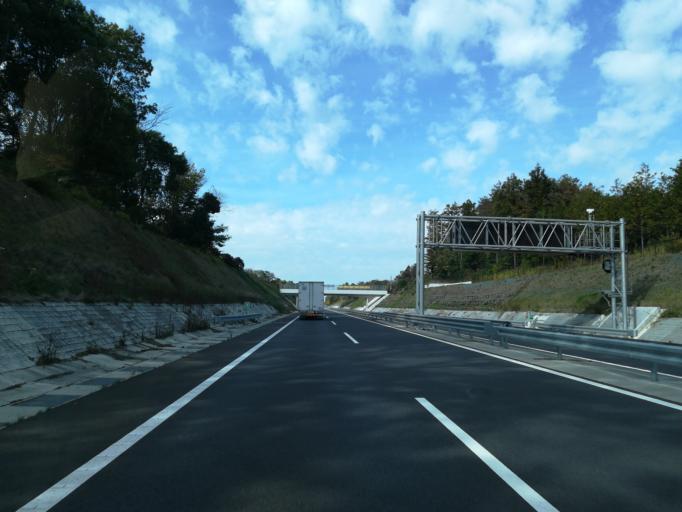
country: JP
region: Ibaraki
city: Mitsukaido
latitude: 36.0639
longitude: 140.0316
